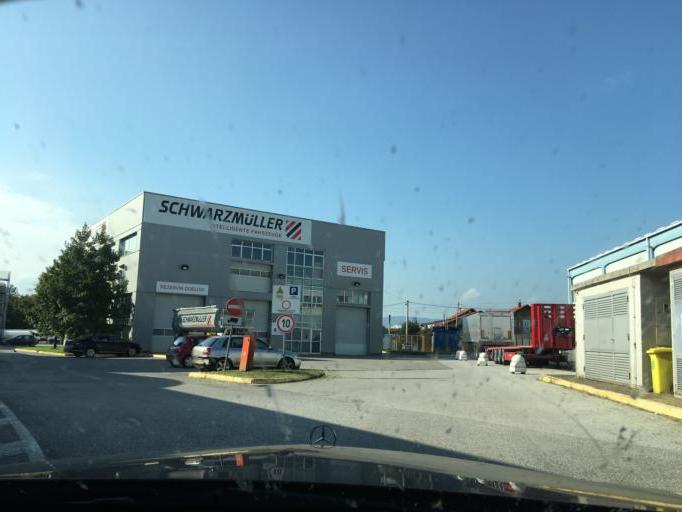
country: HR
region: Grad Zagreb
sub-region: Sesvete
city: Sesvete
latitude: 45.8059
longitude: 16.1098
